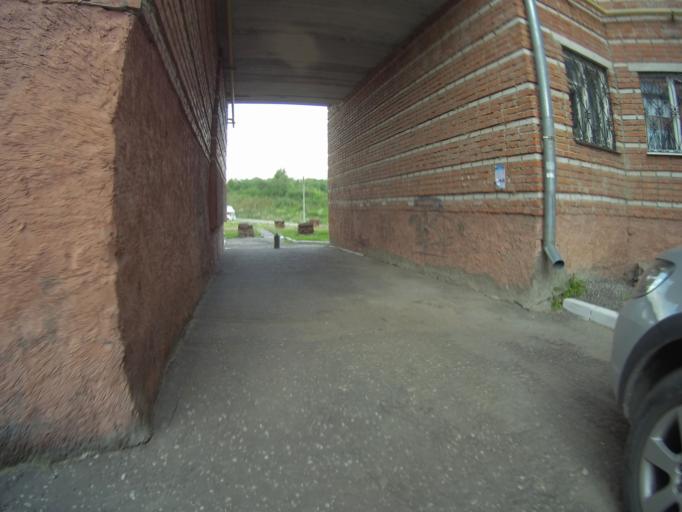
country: RU
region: Vladimir
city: Vladimir
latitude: 56.1322
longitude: 40.3823
